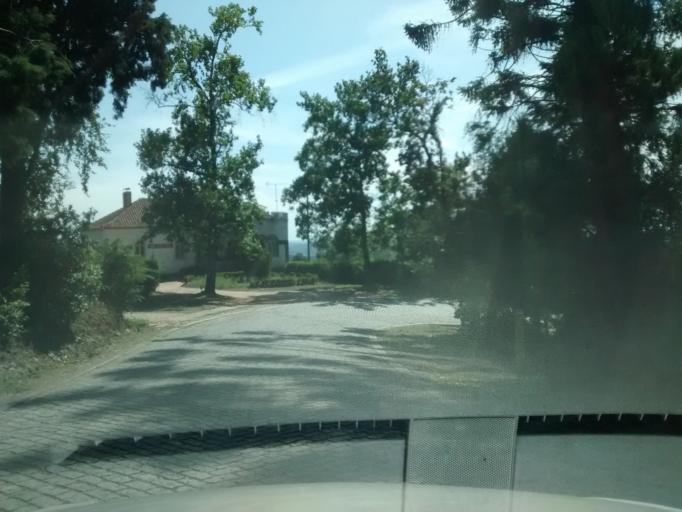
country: PT
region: Aveiro
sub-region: Mealhada
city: Pampilhosa do Botao
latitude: 40.3790
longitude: -8.3754
